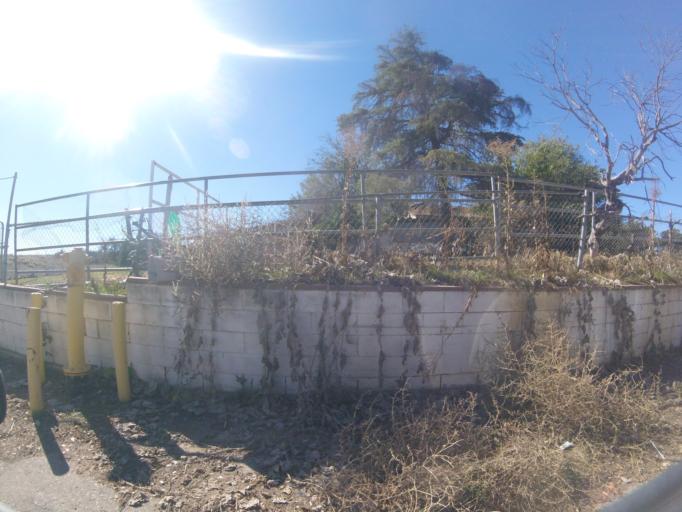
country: US
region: California
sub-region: Riverside County
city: Calimesa
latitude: 34.0206
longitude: -117.1097
